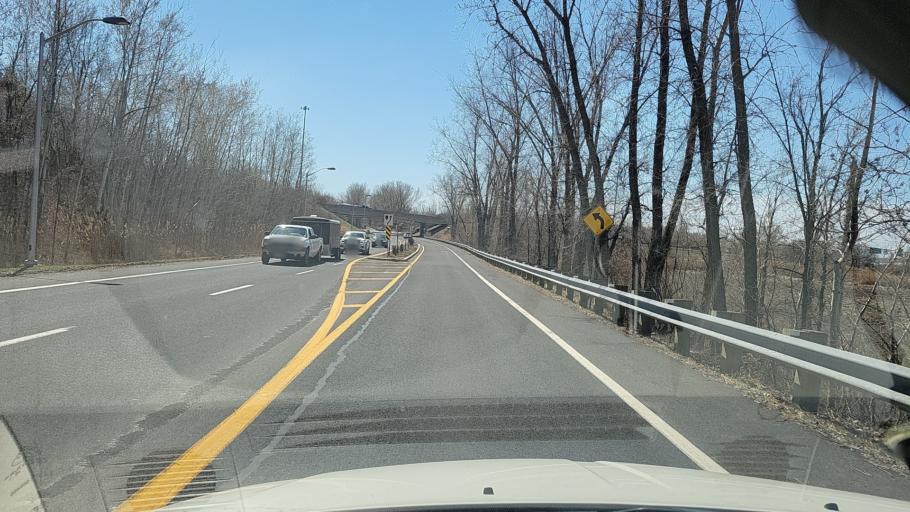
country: CA
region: Quebec
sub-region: Monteregie
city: Sainte-Julie
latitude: 45.5776
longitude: -73.3604
